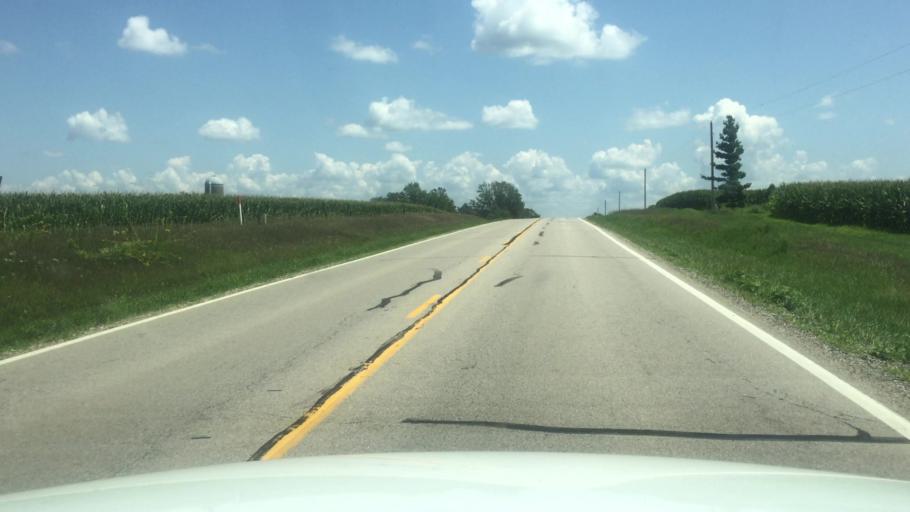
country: US
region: Kansas
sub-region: Brown County
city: Horton
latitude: 39.6674
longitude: -95.5876
